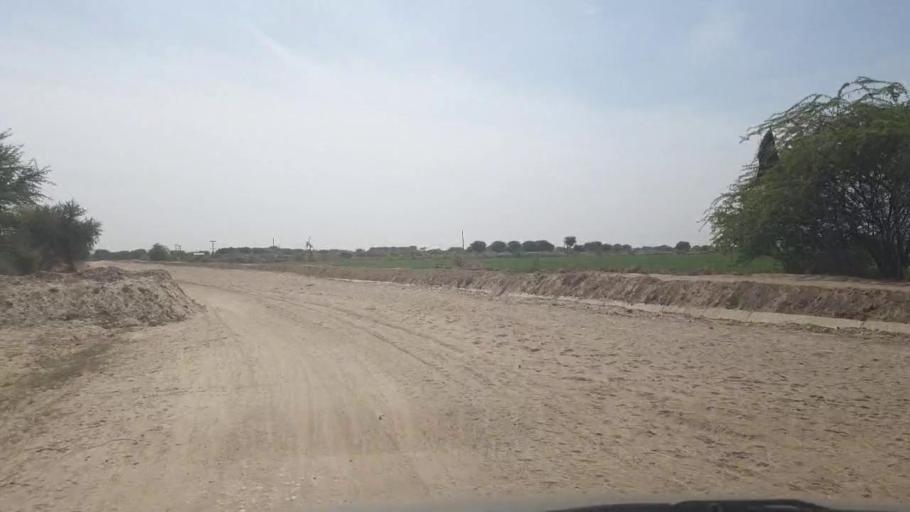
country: PK
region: Sindh
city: Kunri
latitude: 25.2297
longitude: 69.6566
